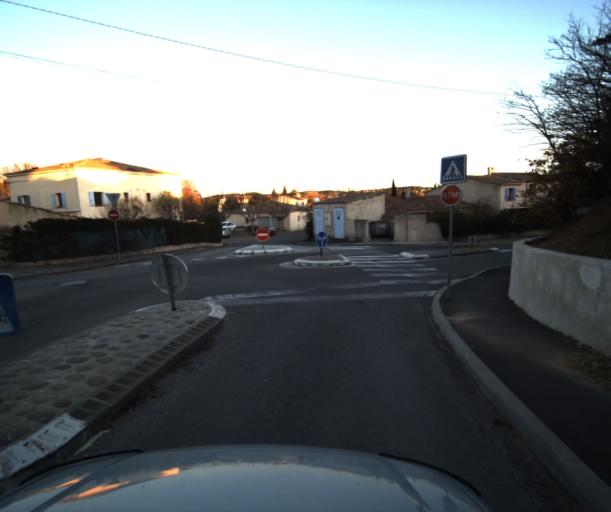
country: FR
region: Provence-Alpes-Cote d'Azur
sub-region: Departement du Vaucluse
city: Pertuis
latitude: 43.7007
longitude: 5.4986
